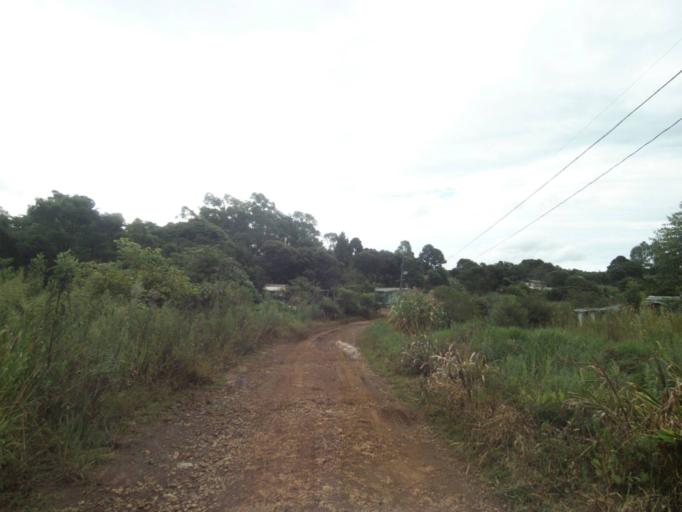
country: BR
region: Parana
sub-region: Pitanga
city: Pitanga
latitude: -24.8981
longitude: -51.9640
